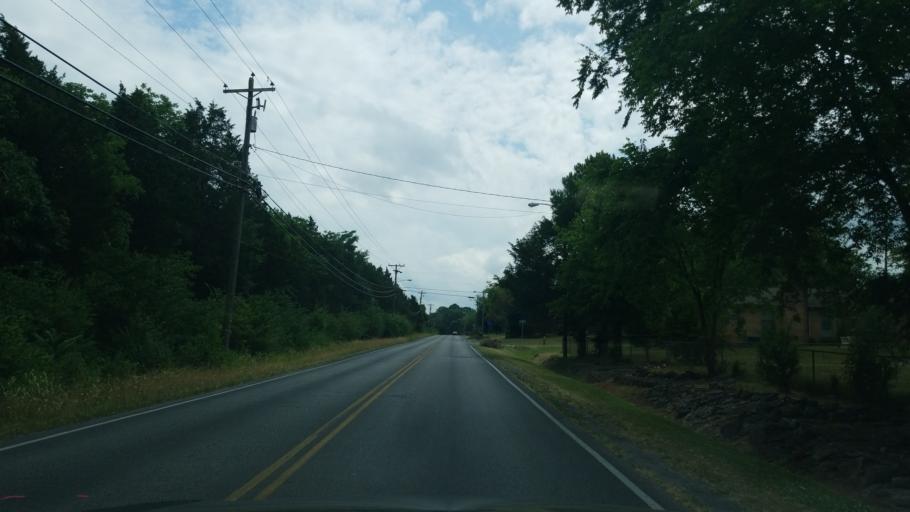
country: US
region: Tennessee
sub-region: Rutherford County
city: La Vergne
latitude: 36.0961
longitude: -86.6038
